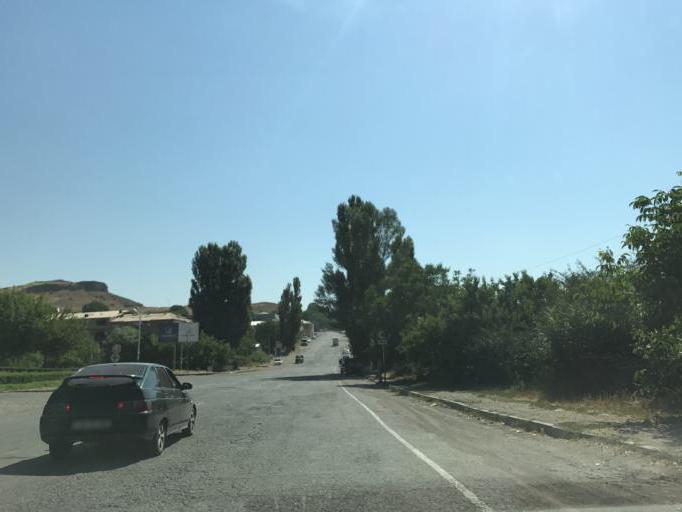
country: AM
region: Vayots' Dzori Marz
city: Yeghegnadzor
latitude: 39.7543
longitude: 45.3319
